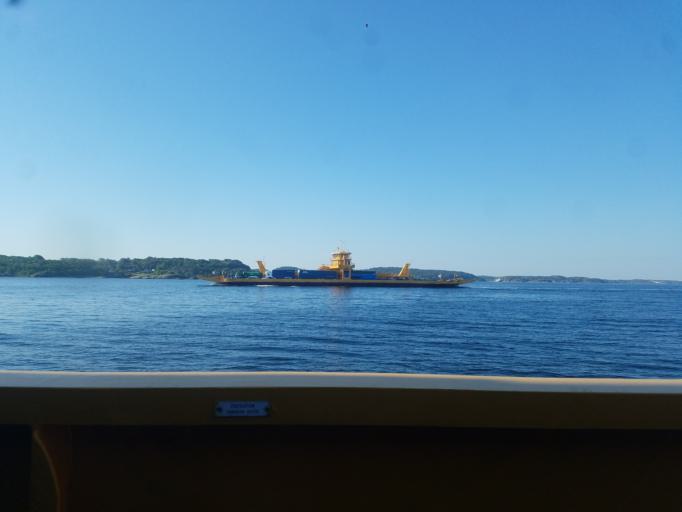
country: SE
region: Vaestra Goetaland
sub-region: Lysekils Kommun
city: Brastad
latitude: 58.3026
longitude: 11.5233
